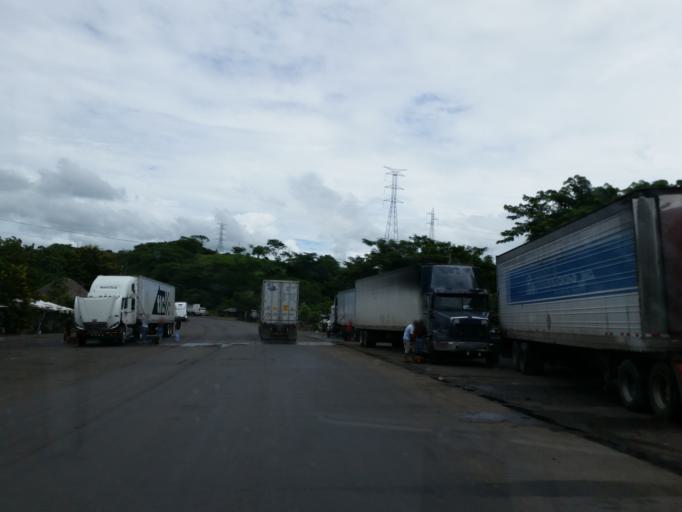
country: NI
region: Chinandega
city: Somotillo
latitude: 12.8609
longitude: -86.8542
